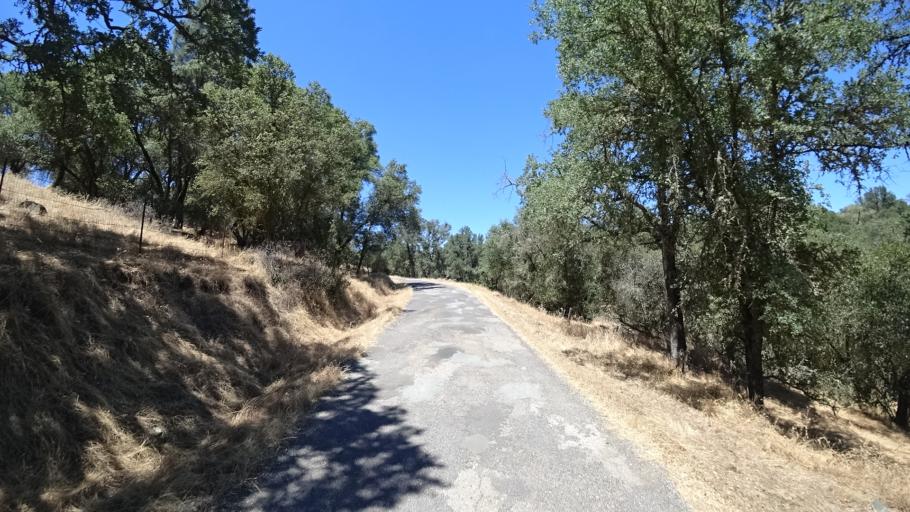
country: US
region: California
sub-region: Calaveras County
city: San Andreas
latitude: 38.2095
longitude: -120.7271
